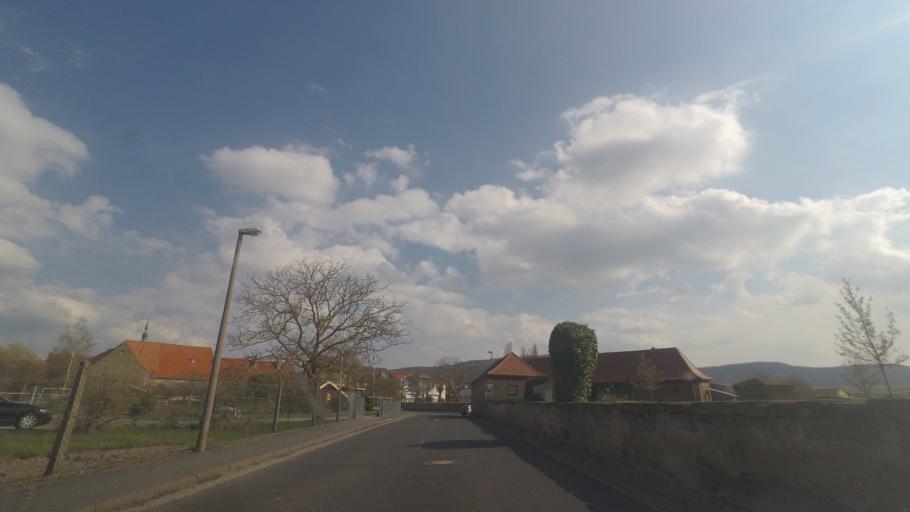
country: DE
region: Bavaria
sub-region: Regierungsbezirk Unterfranken
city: Castell
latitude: 49.7705
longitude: 10.3690
